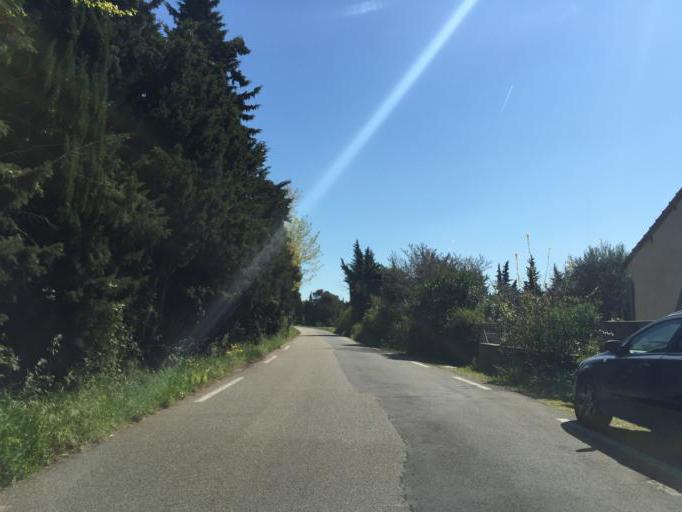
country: FR
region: Provence-Alpes-Cote d'Azur
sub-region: Departement du Vaucluse
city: Orange
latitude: 44.1139
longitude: 4.8018
